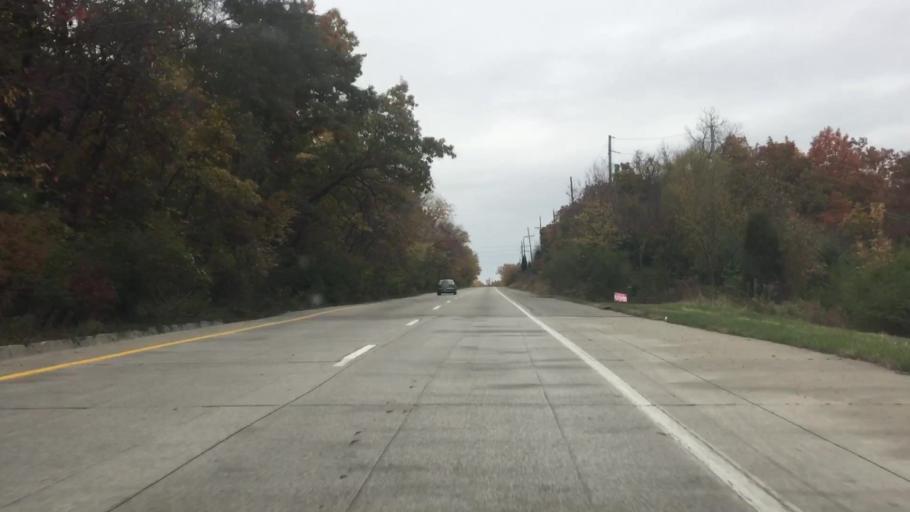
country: US
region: Missouri
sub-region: Jackson County
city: Raytown
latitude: 38.9685
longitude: -94.4362
